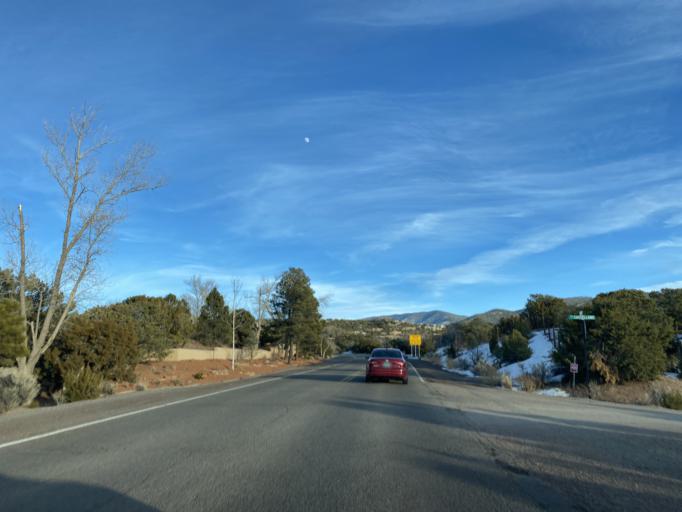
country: US
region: New Mexico
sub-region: Santa Fe County
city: Santa Fe
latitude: 35.6949
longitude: -105.9179
